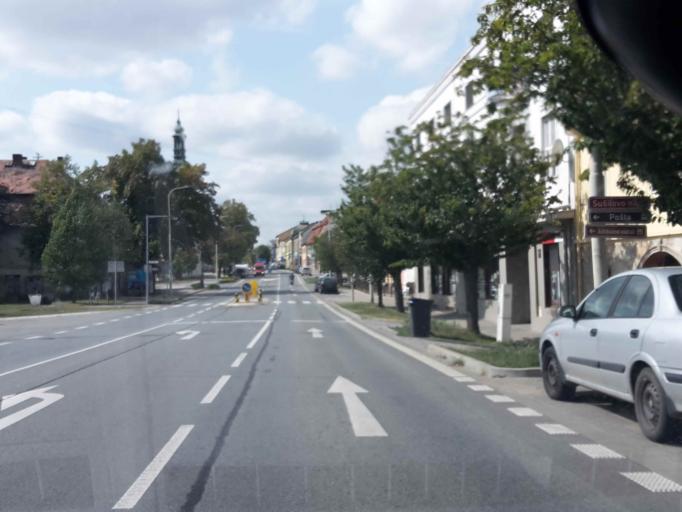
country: CZ
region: South Moravian
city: Rousinov
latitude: 49.2043
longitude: 16.8837
